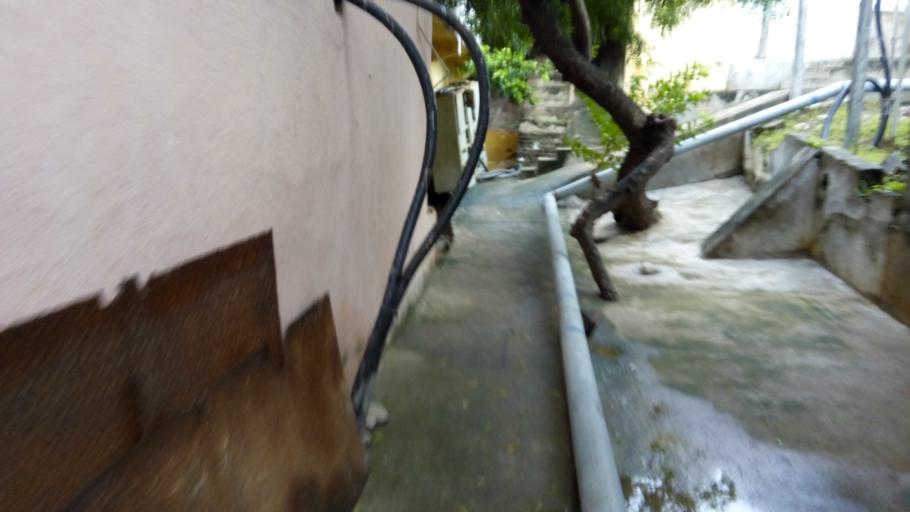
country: IN
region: Andhra Pradesh
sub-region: East Godavari
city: Rajahmundry
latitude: 17.0131
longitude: 81.7700
